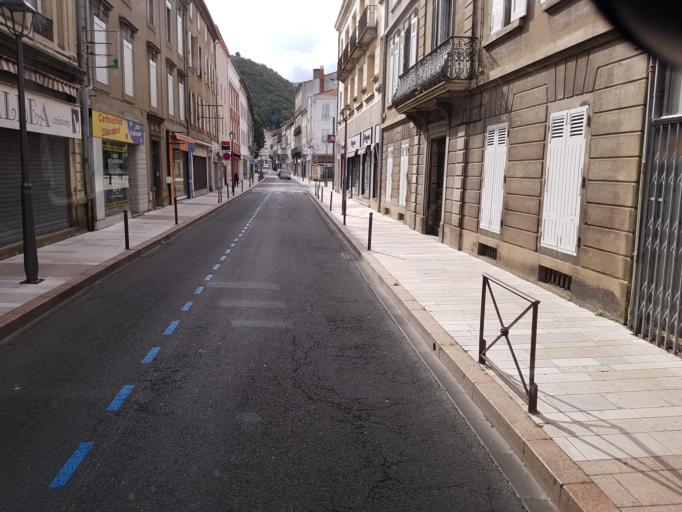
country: FR
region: Midi-Pyrenees
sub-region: Departement du Tarn
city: Mazamet
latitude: 43.4923
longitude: 2.3747
